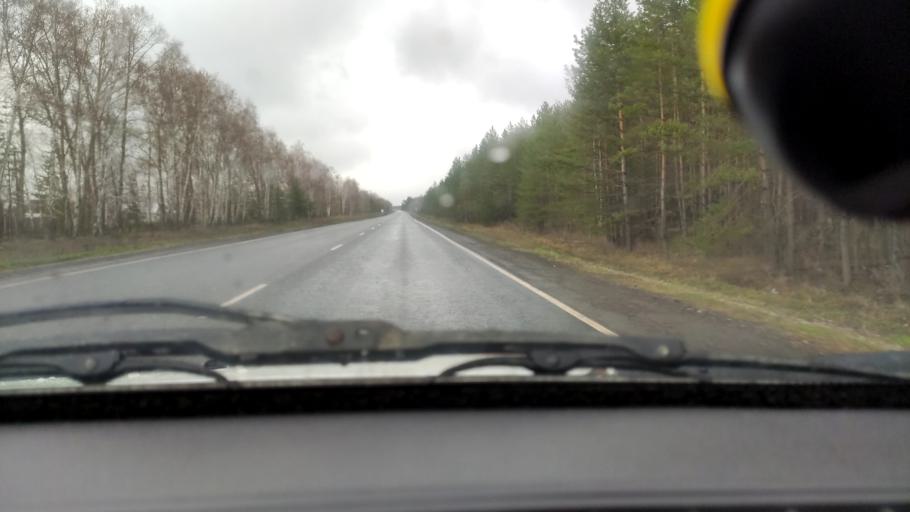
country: RU
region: Samara
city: Povolzhskiy
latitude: 53.6143
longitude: 49.6259
